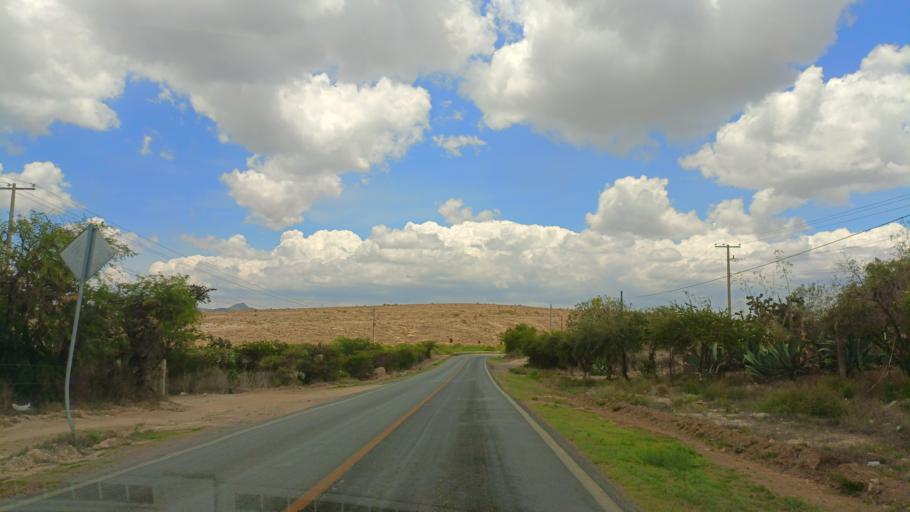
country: MX
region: Guanajuato
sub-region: San Luis de la Paz
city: San Ignacio
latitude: 21.2338
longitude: -100.4903
